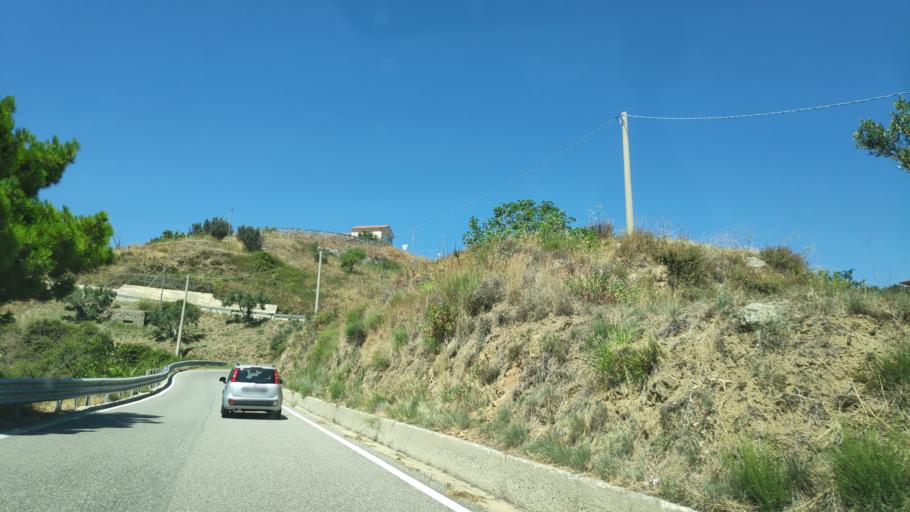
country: IT
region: Calabria
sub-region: Provincia di Catanzaro
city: Montauro
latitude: 38.7467
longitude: 16.5173
